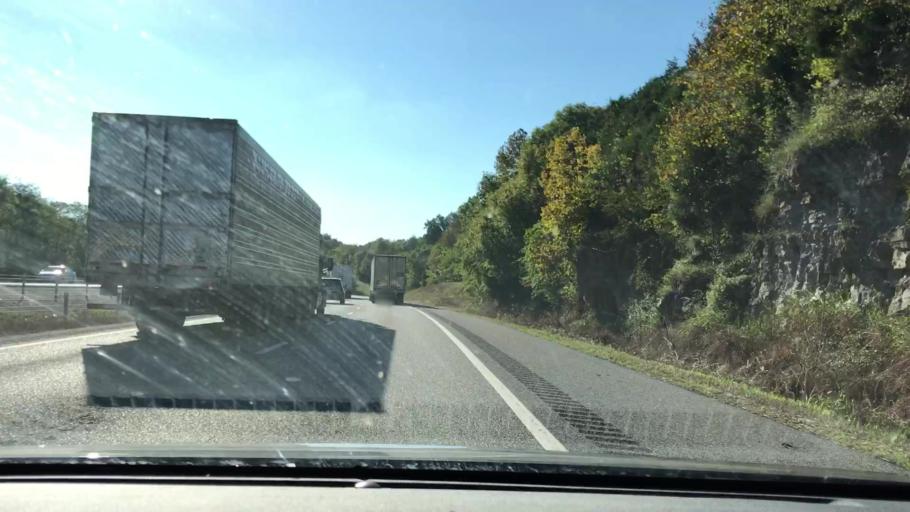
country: US
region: Tennessee
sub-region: Wilson County
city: Watertown
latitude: 36.1755
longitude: -86.0784
